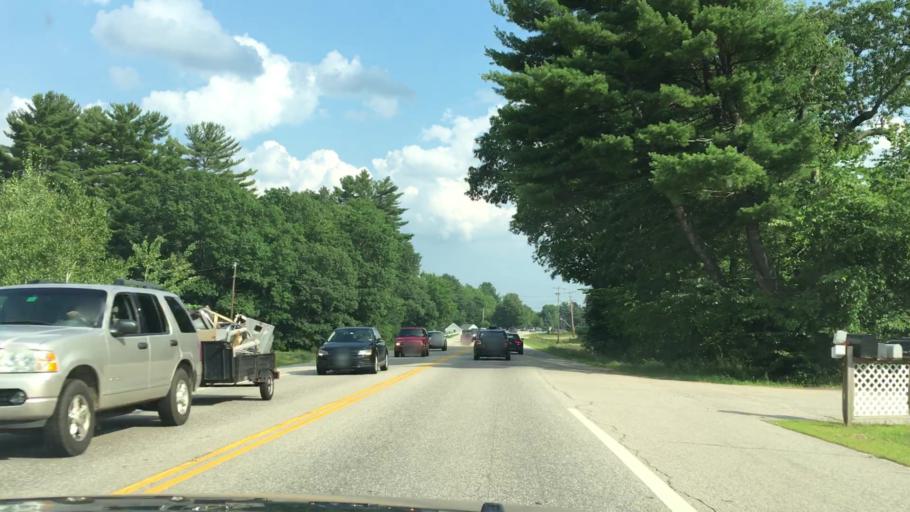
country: US
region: New Hampshire
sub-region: Strafford County
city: Farmington
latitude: 43.3559
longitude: -71.0296
